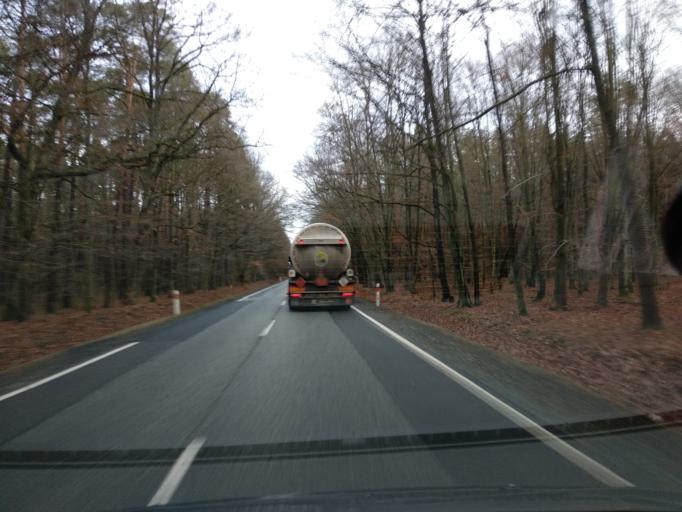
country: PL
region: Lower Silesian Voivodeship
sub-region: Powiat olesnicki
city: Twardogora
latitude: 51.3160
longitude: 17.5561
